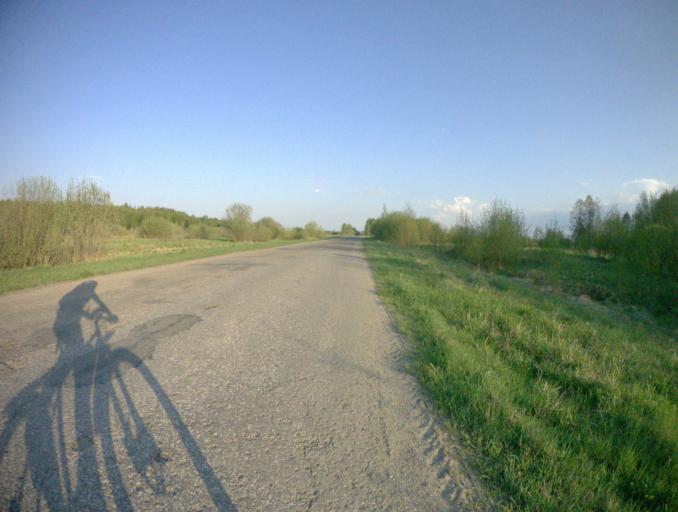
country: RU
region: Vladimir
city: Vyazniki
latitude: 56.3219
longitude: 42.1220
